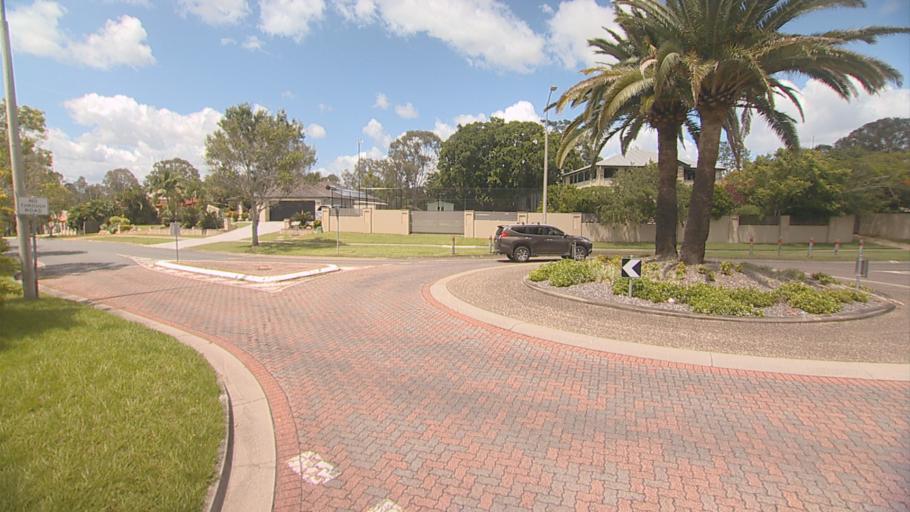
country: AU
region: Queensland
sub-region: Logan
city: Beenleigh
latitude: -27.6980
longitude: 153.1836
